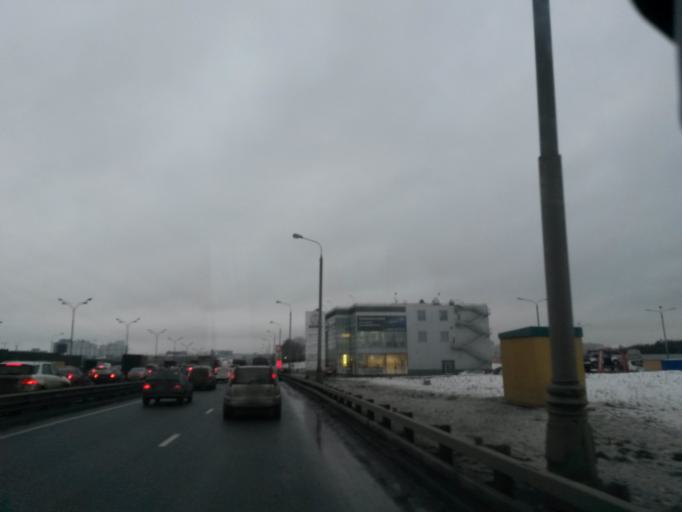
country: RU
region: Moskovskaya
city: Zarech'ye
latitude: 55.6939
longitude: 37.4104
